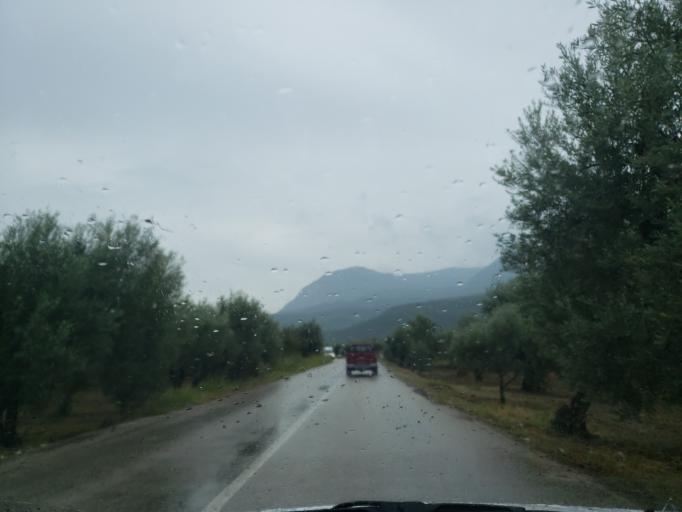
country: GR
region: Central Greece
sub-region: Nomos Fthiotidos
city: Anthili
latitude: 38.8028
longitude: 22.4574
